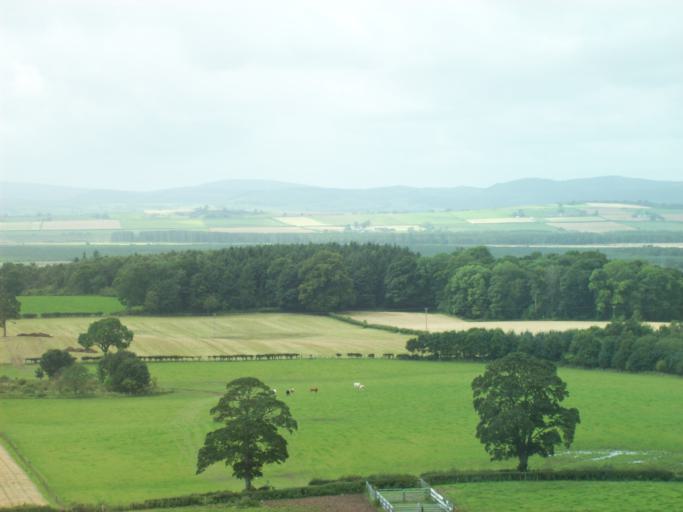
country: GB
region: Scotland
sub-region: Dumfries and Galloway
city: Lochmaben
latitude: 55.0551
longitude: -3.4699
